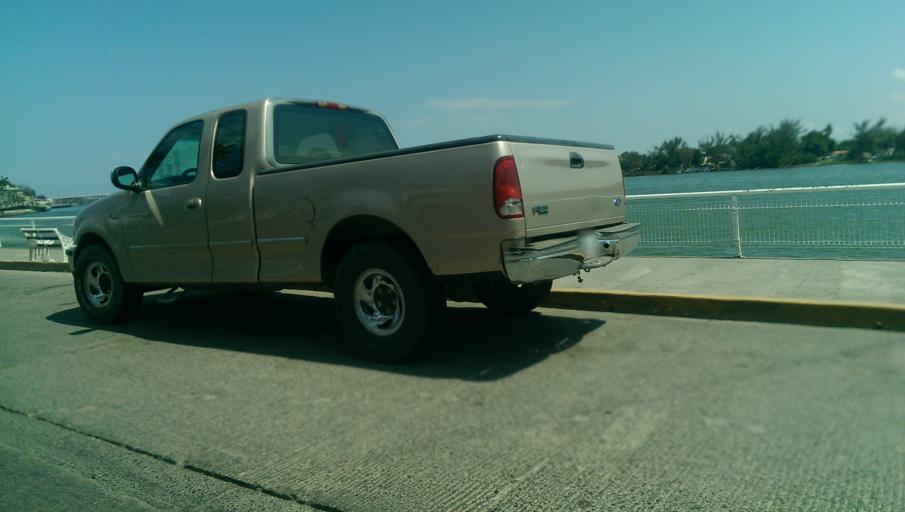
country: MX
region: Veracruz
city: Tuxpan de Rodriguez Cano
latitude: 20.9531
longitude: -97.4097
